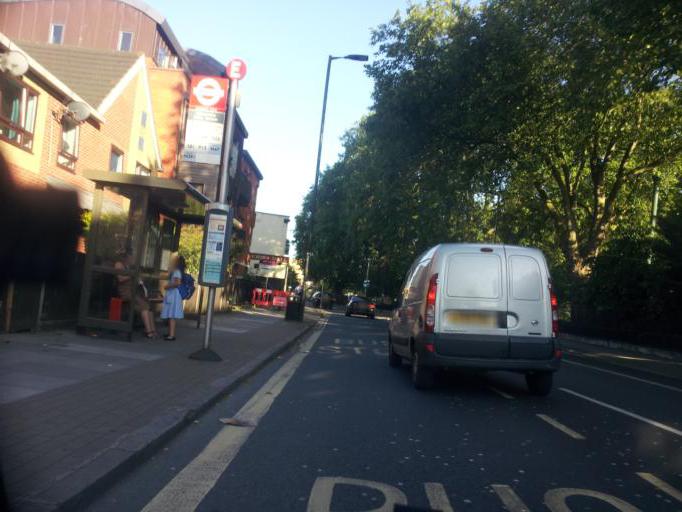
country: GB
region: England
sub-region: Greater London
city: Bethnal Green
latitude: 51.4950
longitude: -0.0506
